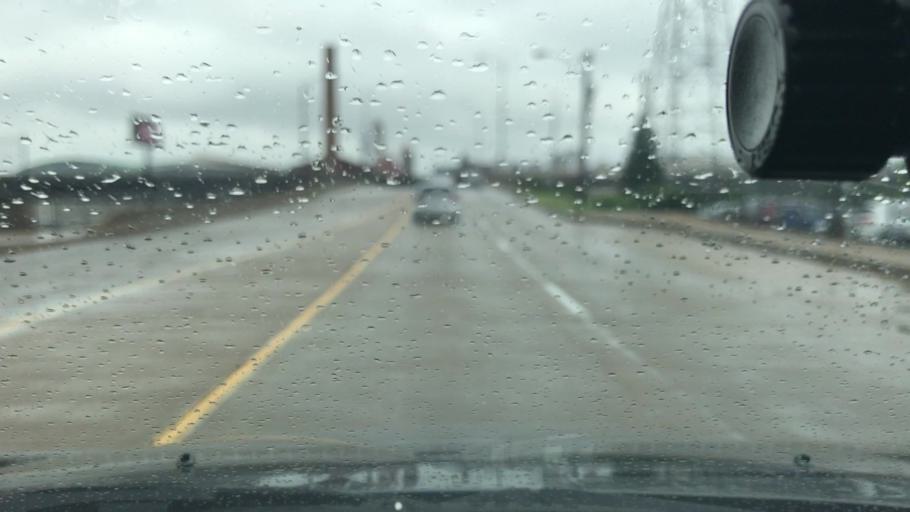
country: US
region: Missouri
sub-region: City of Saint Louis
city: St. Louis
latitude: 38.6226
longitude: -90.2084
